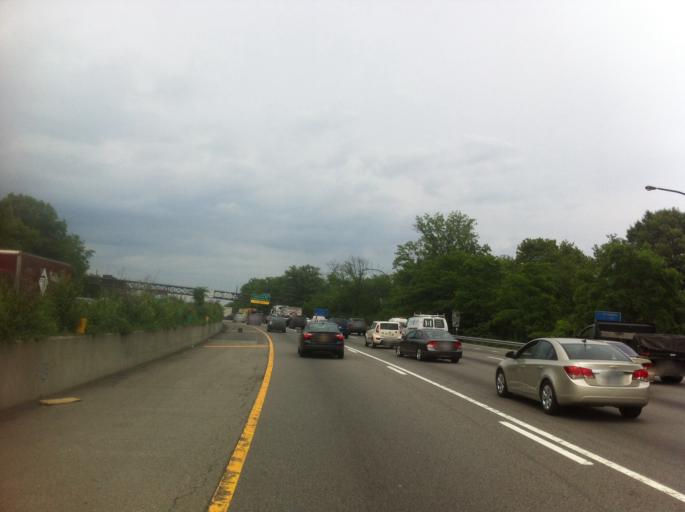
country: US
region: New York
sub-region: Nassau County
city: Lake Success
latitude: 40.7655
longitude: -73.7178
